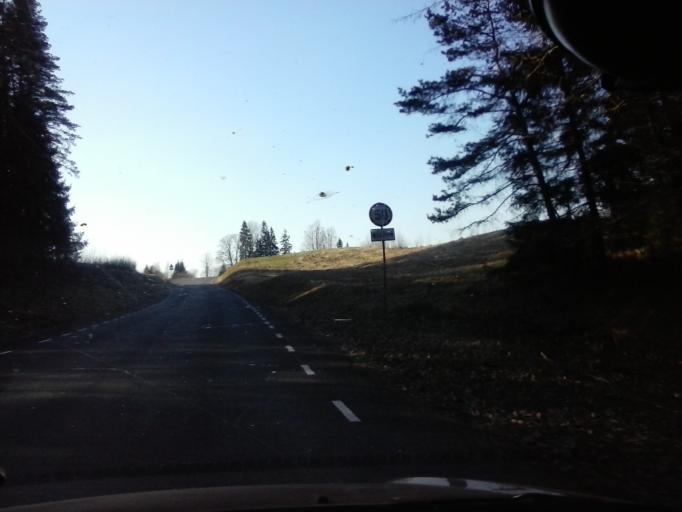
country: EE
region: Tartu
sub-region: UElenurme vald
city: Ulenurme
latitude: 58.1550
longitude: 26.8600
